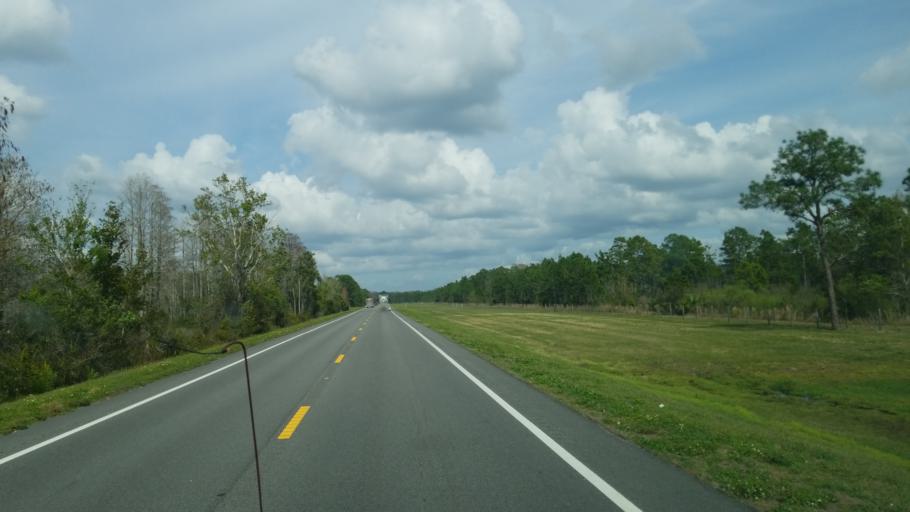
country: US
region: Florida
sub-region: Indian River County
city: Fellsmere
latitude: 27.7399
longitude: -80.9061
